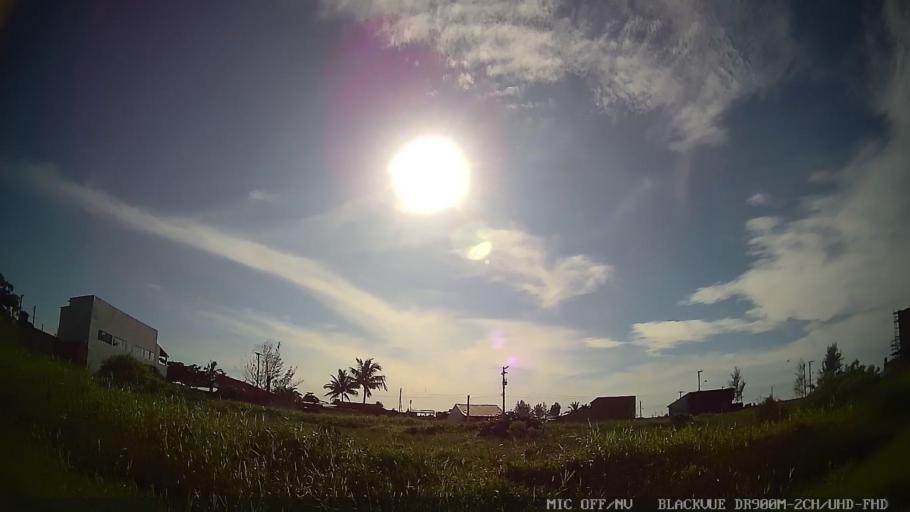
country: BR
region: Sao Paulo
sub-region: Iguape
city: Iguape
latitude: -24.7624
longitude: -47.5759
